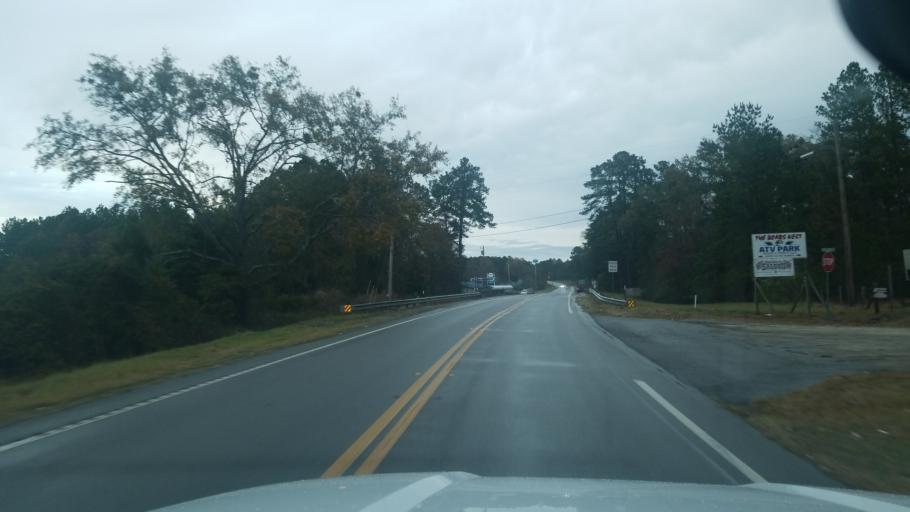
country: US
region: Georgia
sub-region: Coffee County
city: Broxton
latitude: 31.8034
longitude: -82.9835
